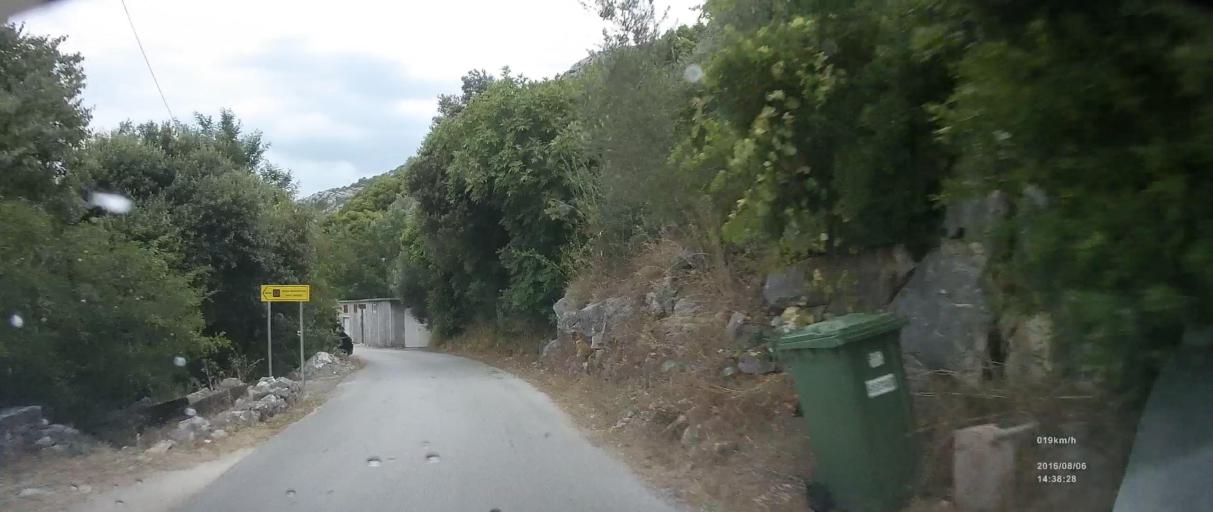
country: HR
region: Dubrovacko-Neretvanska
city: Ston
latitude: 42.7150
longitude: 17.6686
